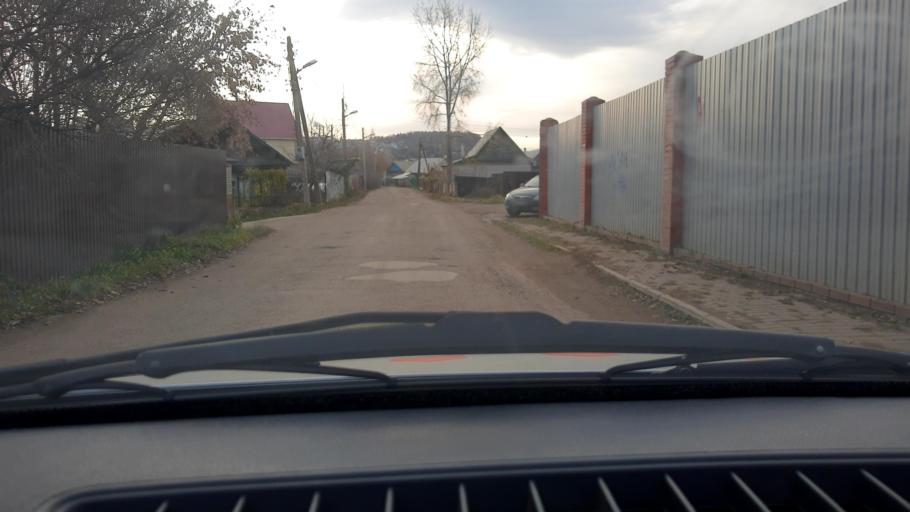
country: RU
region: Bashkortostan
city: Ufa
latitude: 54.7387
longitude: 55.9053
